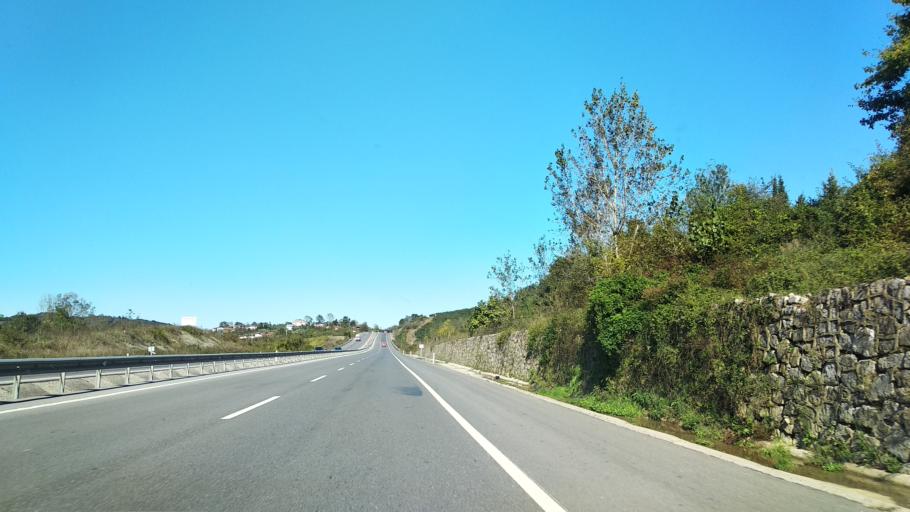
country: TR
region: Sakarya
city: Ortakoy
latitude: 41.0401
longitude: 30.6209
